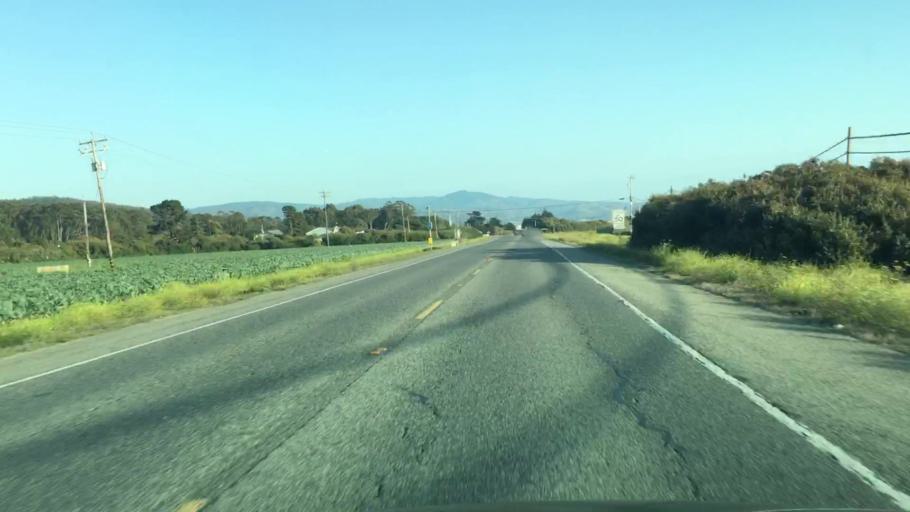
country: US
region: California
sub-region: San Mateo County
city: El Granada
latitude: 37.5119
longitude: -122.4914
